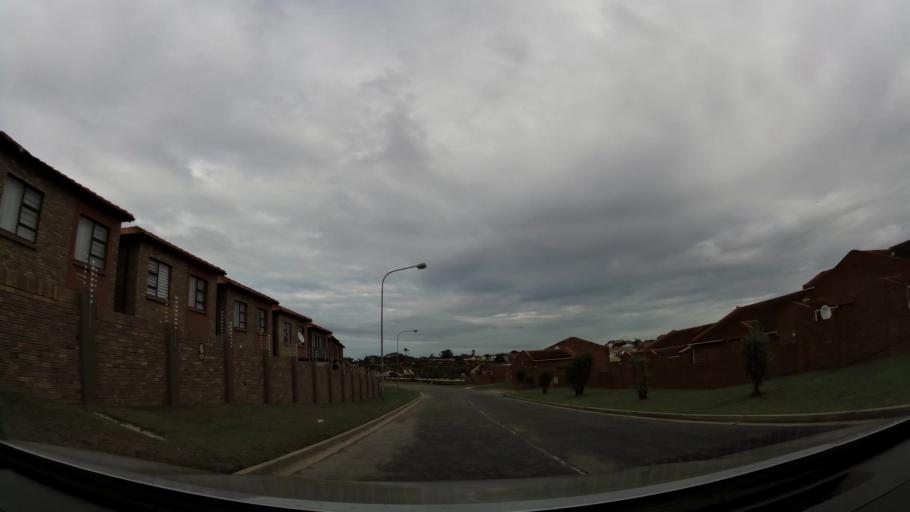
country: ZA
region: Eastern Cape
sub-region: Nelson Mandela Bay Metropolitan Municipality
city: Port Elizabeth
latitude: -33.9709
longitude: 25.6210
